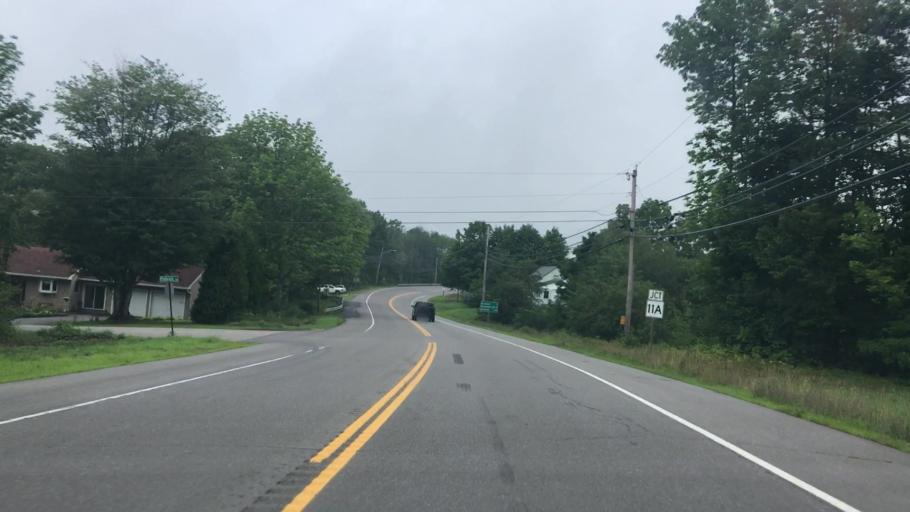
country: US
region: Maine
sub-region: York County
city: Lebanon
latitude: 43.4253
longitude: -70.8285
